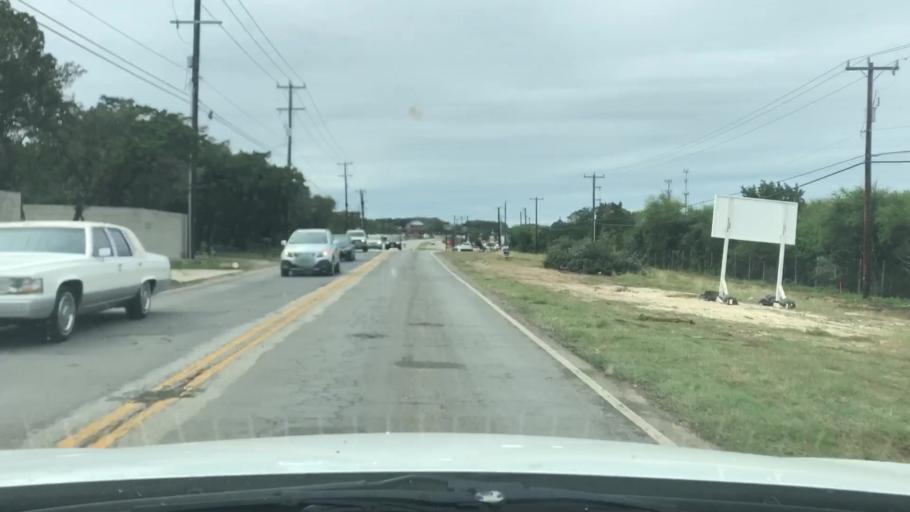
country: US
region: Texas
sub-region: Bexar County
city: Timberwood Park
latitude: 29.6480
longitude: -98.4209
